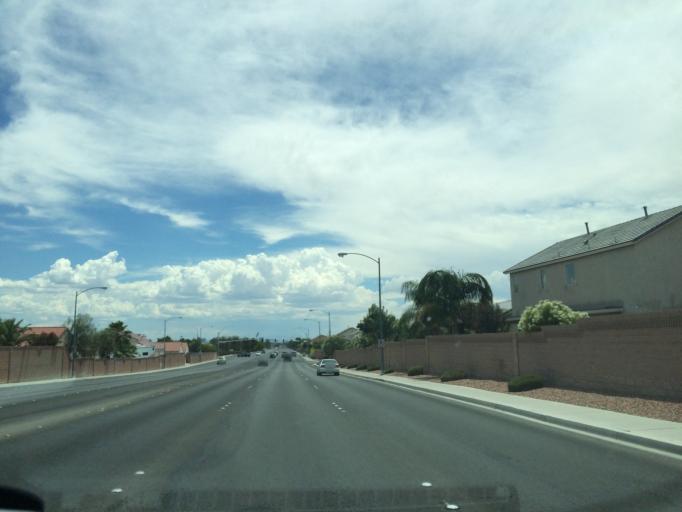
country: US
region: Nevada
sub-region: Clark County
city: North Las Vegas
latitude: 36.2715
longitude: -115.1799
